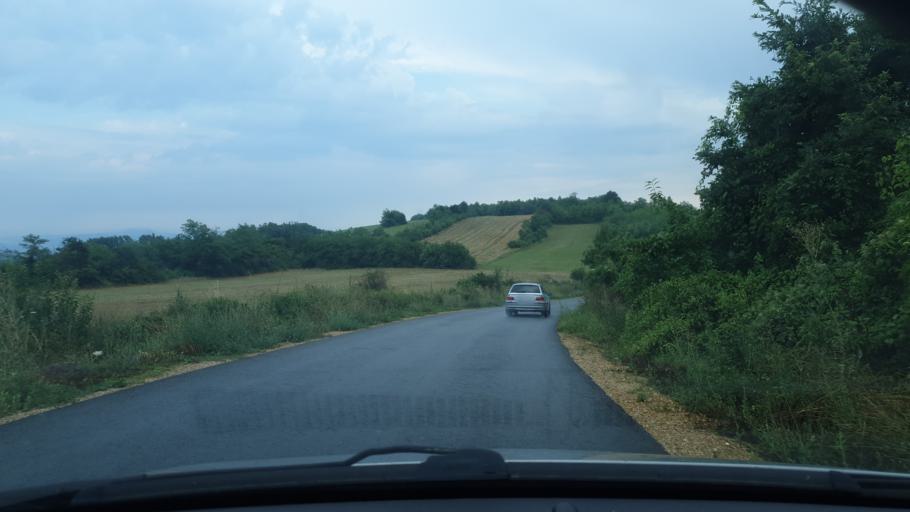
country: RS
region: Central Serbia
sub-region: Sumadijski Okrug
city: Kragujevac
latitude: 44.0584
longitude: 20.7849
